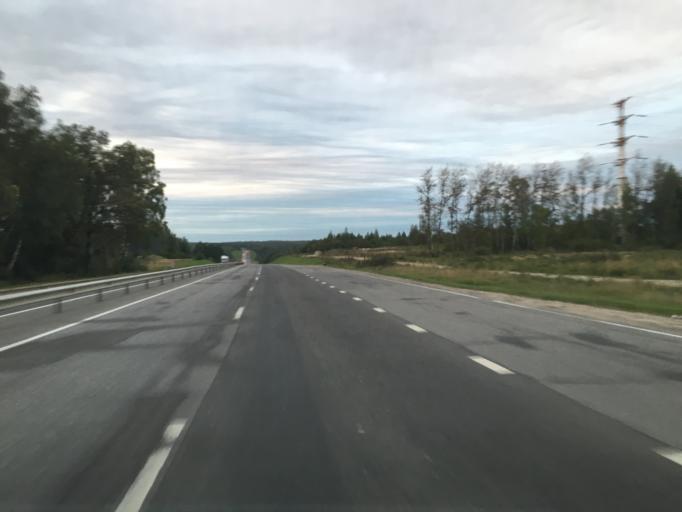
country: RU
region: Kaluga
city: Kaluga
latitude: 54.5902
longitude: 36.3301
